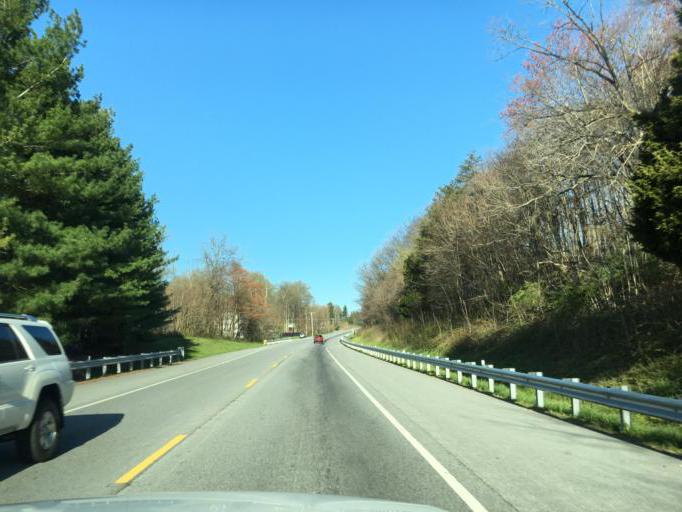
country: US
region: Maryland
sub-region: Carroll County
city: New Windsor
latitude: 39.4605
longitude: -77.1016
